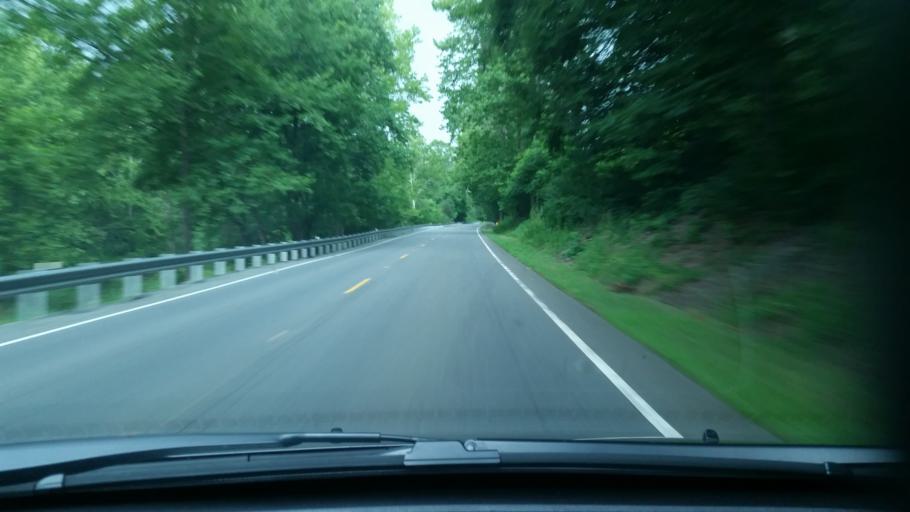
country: US
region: Virginia
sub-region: Nelson County
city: Nellysford
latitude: 37.9019
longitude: -78.8323
